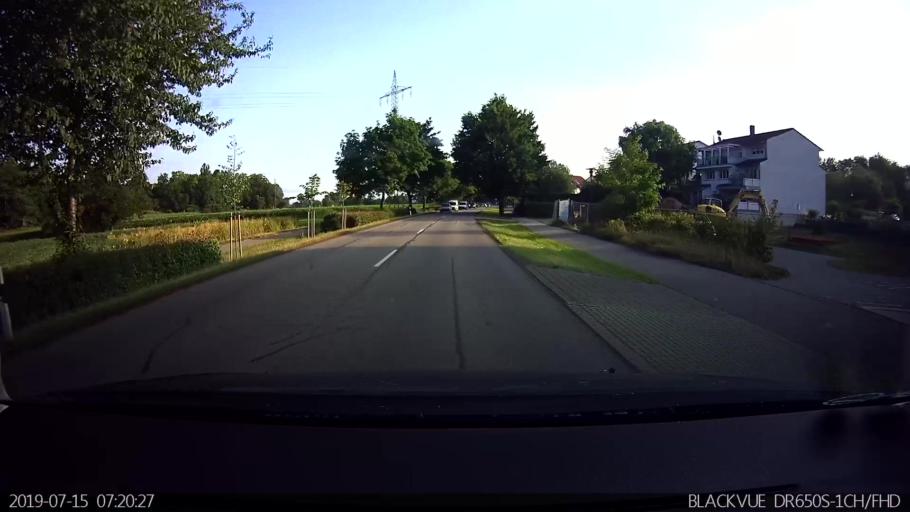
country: DE
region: Baden-Wuerttemberg
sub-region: Freiburg Region
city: Unterkrozingen
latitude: 47.9214
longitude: 7.6850
